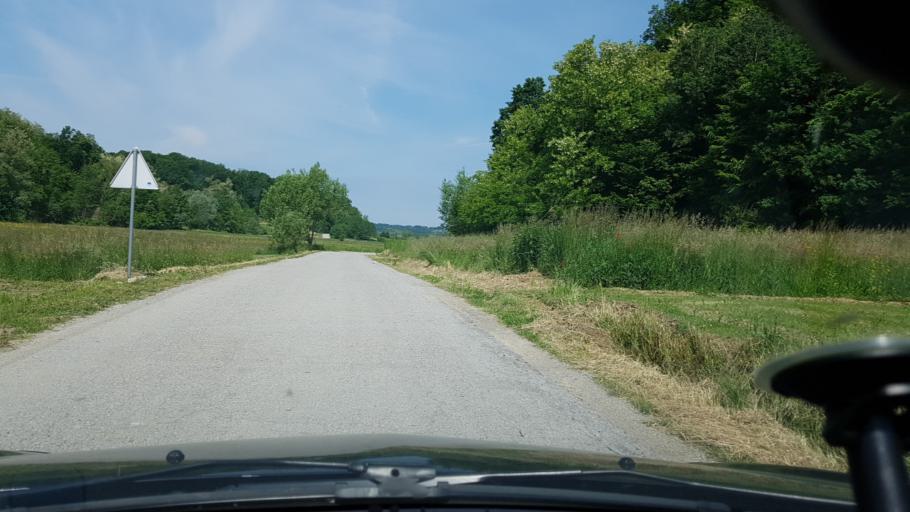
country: HR
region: Krapinsko-Zagorska
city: Selnica
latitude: 46.0303
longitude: 16.0333
